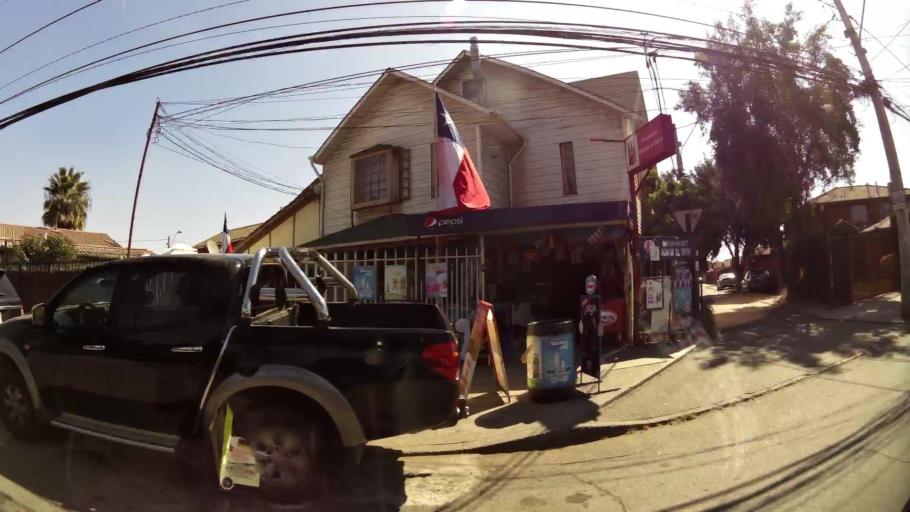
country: CL
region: Santiago Metropolitan
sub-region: Provincia de Santiago
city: Lo Prado
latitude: -33.3509
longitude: -70.7324
